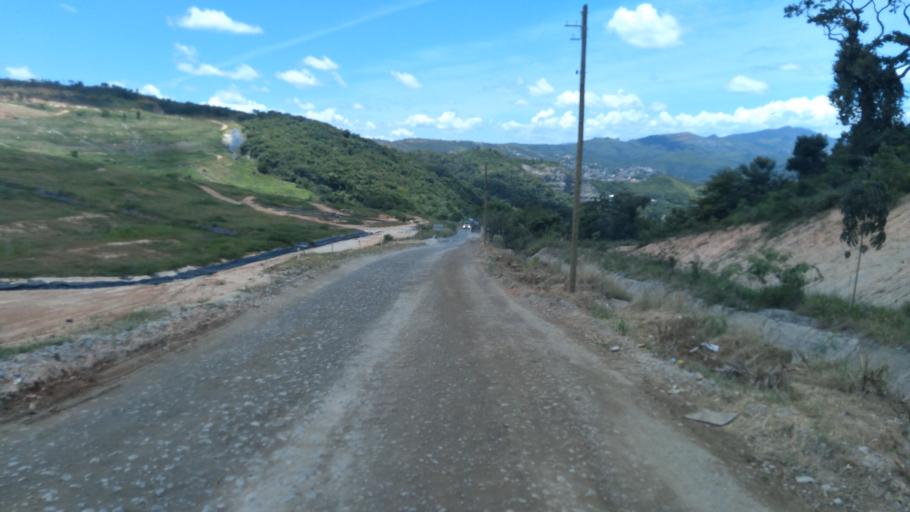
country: BR
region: Minas Gerais
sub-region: Santa Luzia
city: Santa Luzia
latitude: -19.8522
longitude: -43.8499
